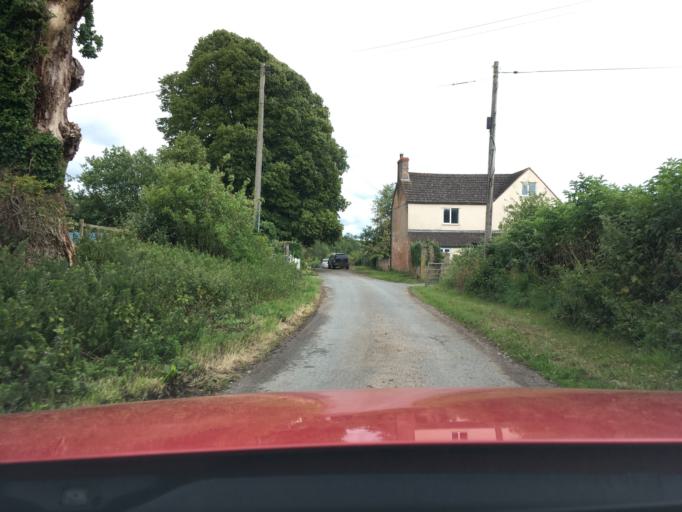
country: GB
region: England
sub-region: Gloucestershire
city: Cinderford
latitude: 51.8004
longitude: -2.4174
